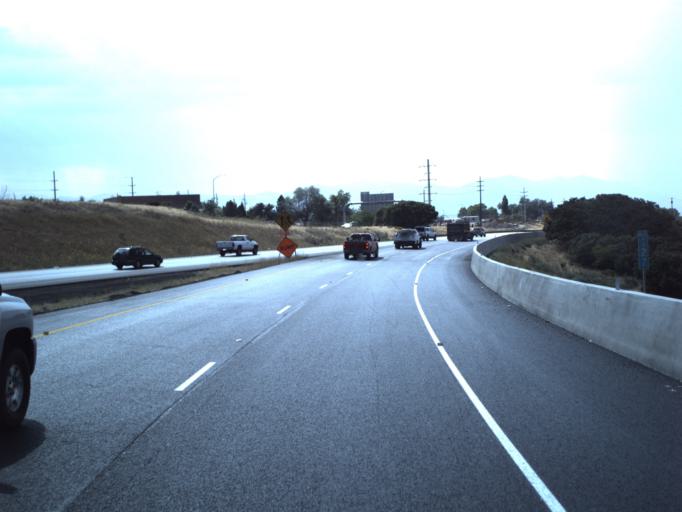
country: US
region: Utah
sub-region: Salt Lake County
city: Canyon Rim
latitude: 40.7133
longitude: -111.8185
